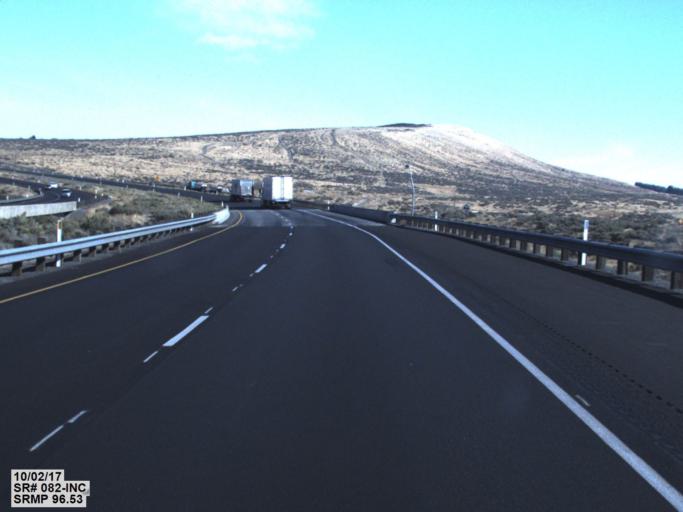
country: US
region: Washington
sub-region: Benton County
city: Benton City
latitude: 46.2510
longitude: -119.4770
